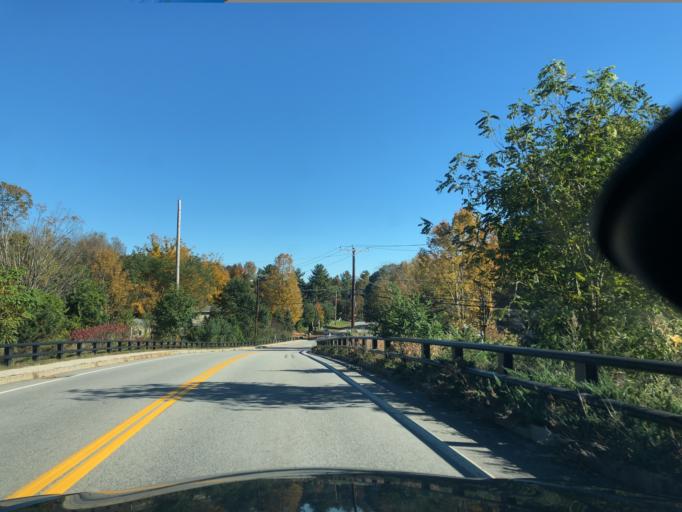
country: US
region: New Hampshire
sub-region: Rockingham County
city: Stratham Station
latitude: 43.0387
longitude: -70.9362
